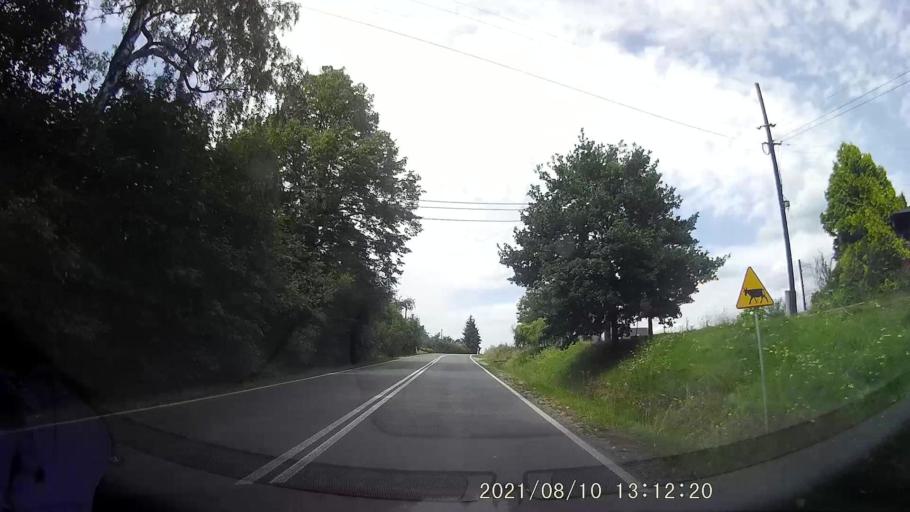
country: PL
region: Lower Silesian Voivodeship
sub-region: Powiat klodzki
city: Bozkow
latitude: 50.5147
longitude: 16.5141
